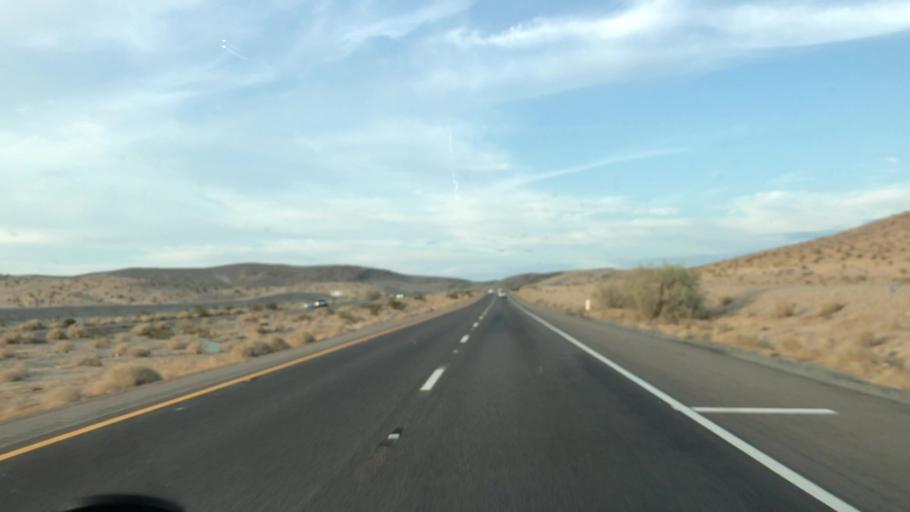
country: US
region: California
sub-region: San Bernardino County
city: Fort Irwin
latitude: 35.0745
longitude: -116.4065
